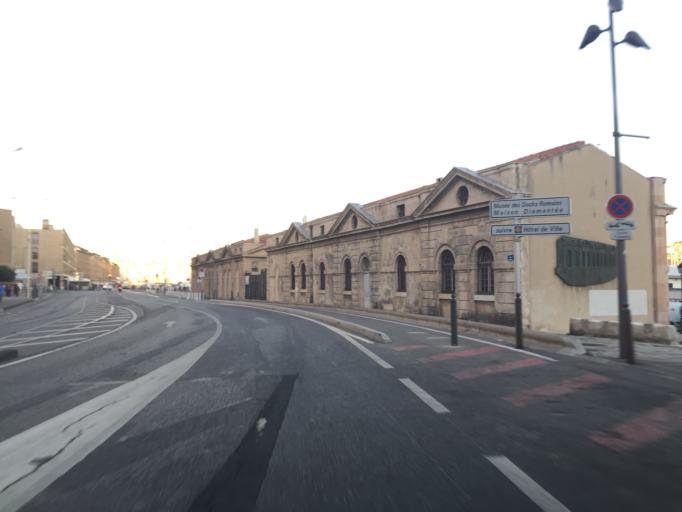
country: FR
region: Provence-Alpes-Cote d'Azur
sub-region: Departement des Bouches-du-Rhone
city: Marseille 02
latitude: 43.2951
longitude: 5.3634
